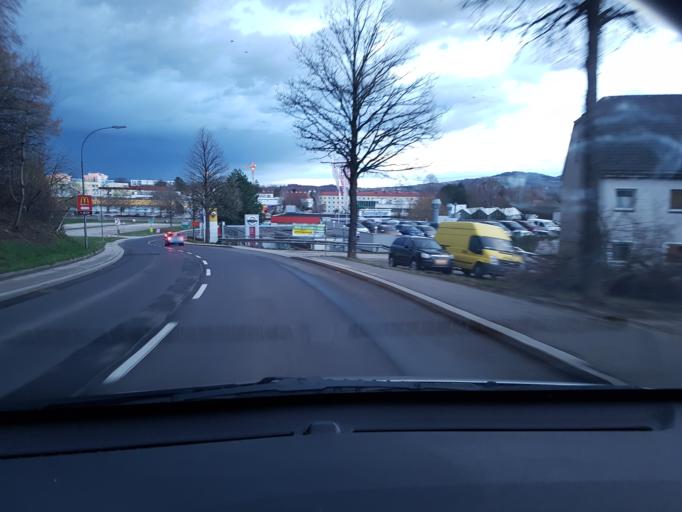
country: AT
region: Upper Austria
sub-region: Steyr Stadt
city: Steyr
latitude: 48.0472
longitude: 14.4112
